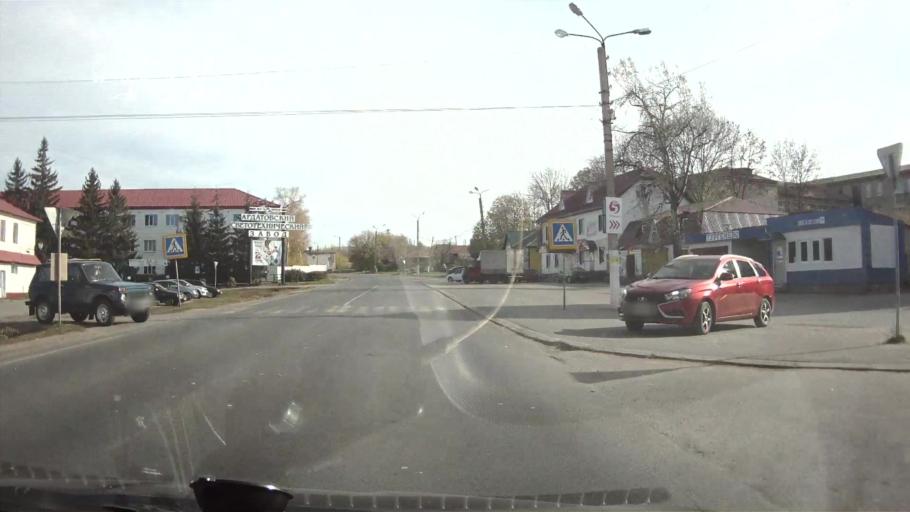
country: RU
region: Mordoviya
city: Turgenevo
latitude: 54.8462
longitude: 46.3373
